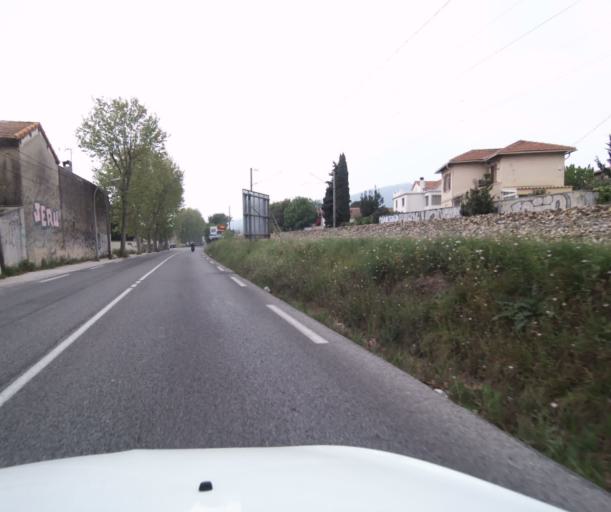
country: FR
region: Provence-Alpes-Cote d'Azur
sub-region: Departement du Var
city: La Garde
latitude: 43.1147
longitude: 5.9865
